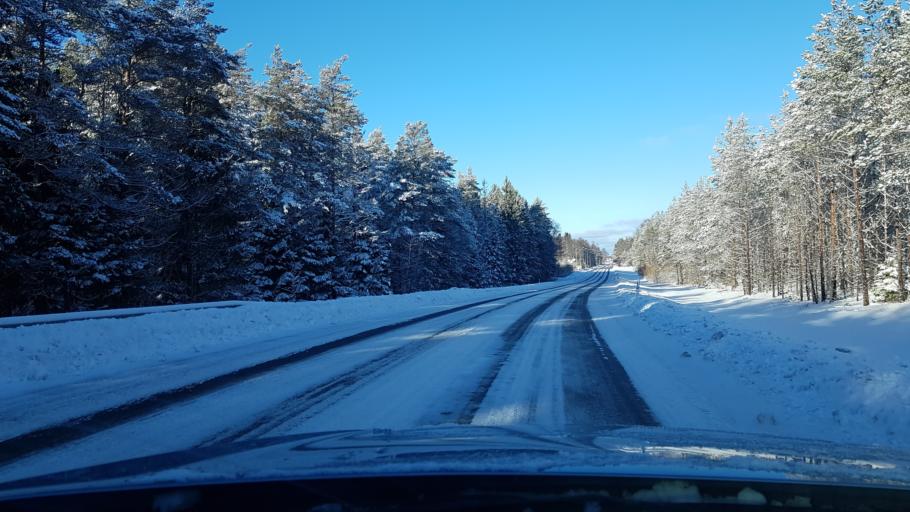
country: EE
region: Hiiumaa
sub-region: Kaerdla linn
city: Kardla
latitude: 58.9752
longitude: 22.7622
